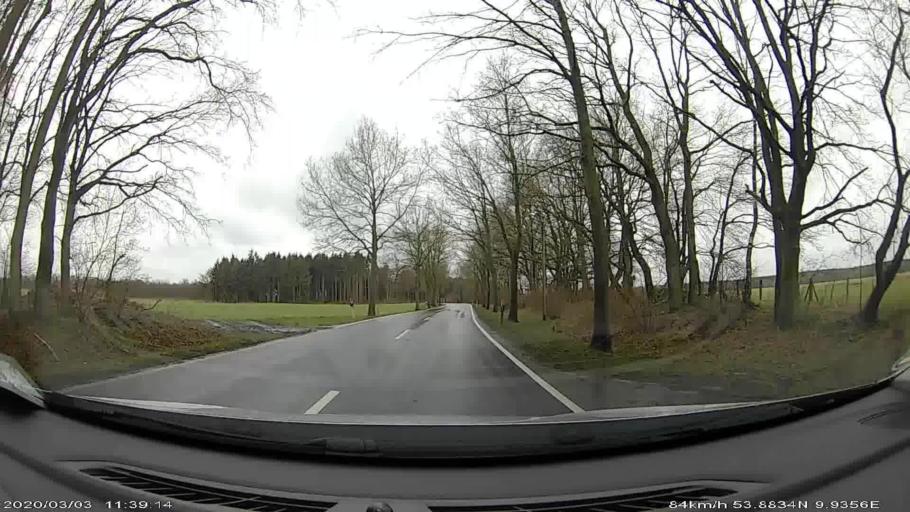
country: DE
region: Schleswig-Holstein
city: Nutzen
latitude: 53.8845
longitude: 9.9312
